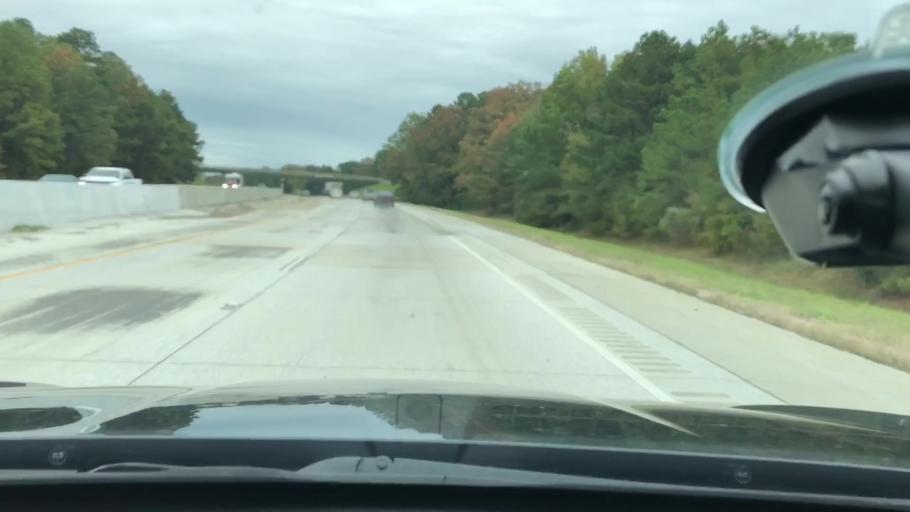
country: US
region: Arkansas
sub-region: Hempstead County
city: Hope
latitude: 33.6093
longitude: -93.8017
